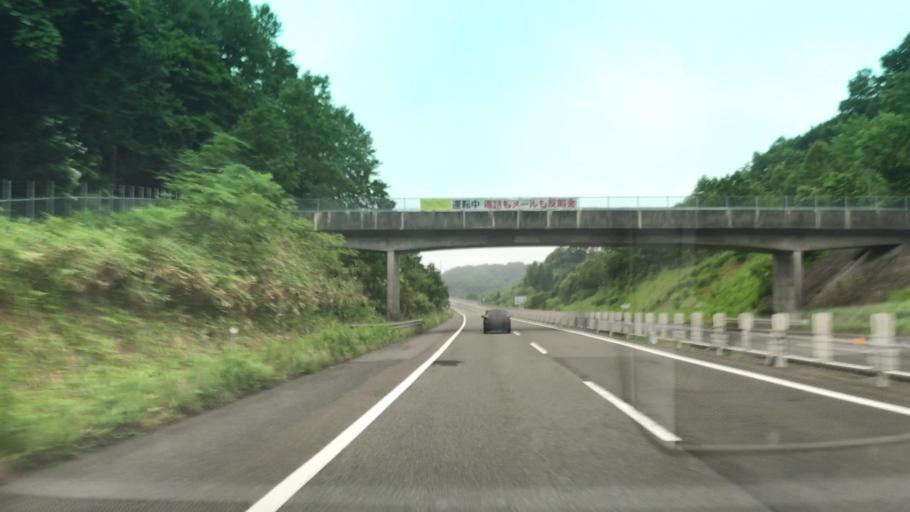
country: JP
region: Hokkaido
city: Shiraoi
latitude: 42.4685
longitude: 141.1966
